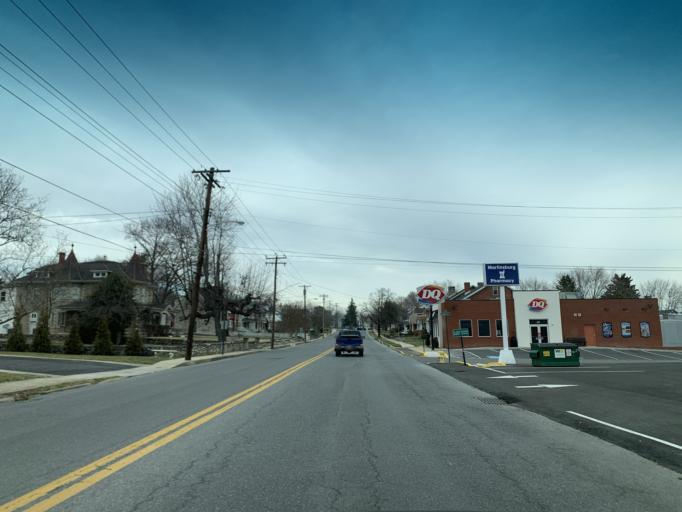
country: US
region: West Virginia
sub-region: Berkeley County
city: Martinsburg
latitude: 39.4484
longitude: -77.9797
